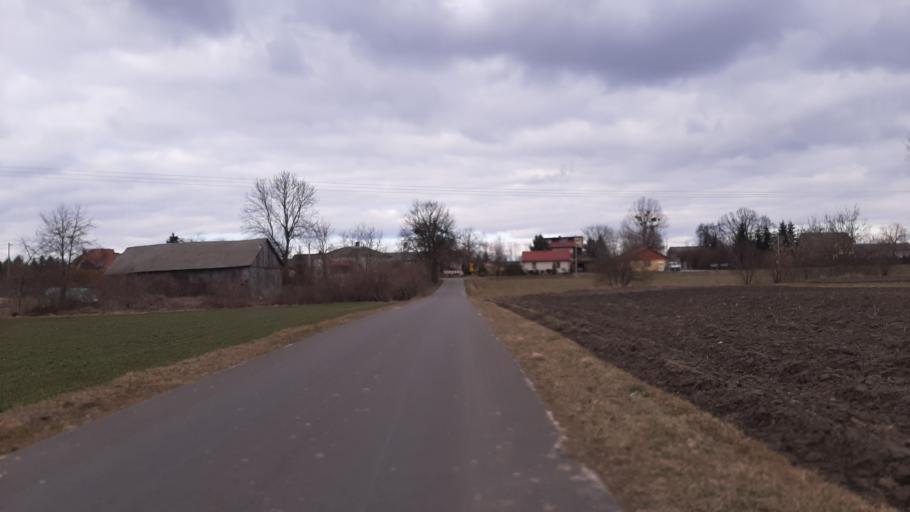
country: PL
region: Lublin Voivodeship
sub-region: Powiat lubelski
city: Jastkow
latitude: 51.3516
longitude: 22.3931
